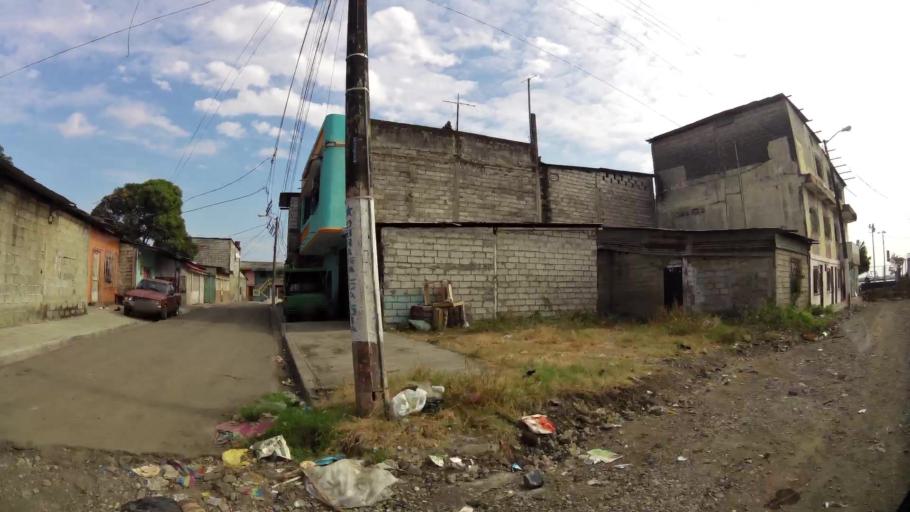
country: EC
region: Guayas
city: Guayaquil
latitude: -2.2509
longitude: -79.8762
